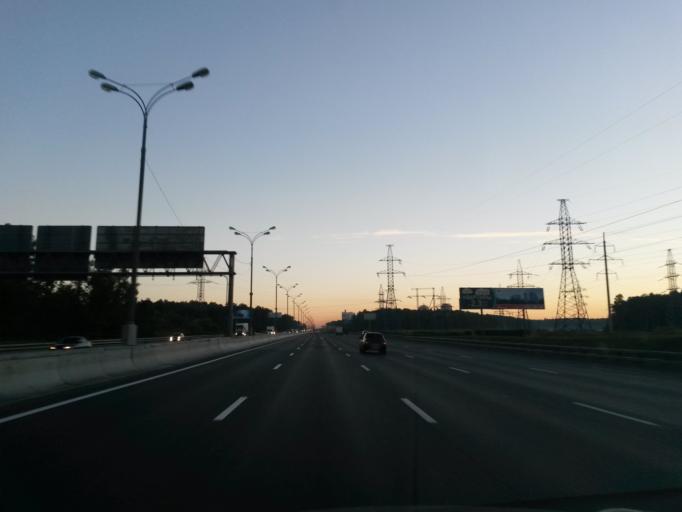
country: RU
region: Moscow
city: Ivanovskoye
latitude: 55.7851
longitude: 37.8419
